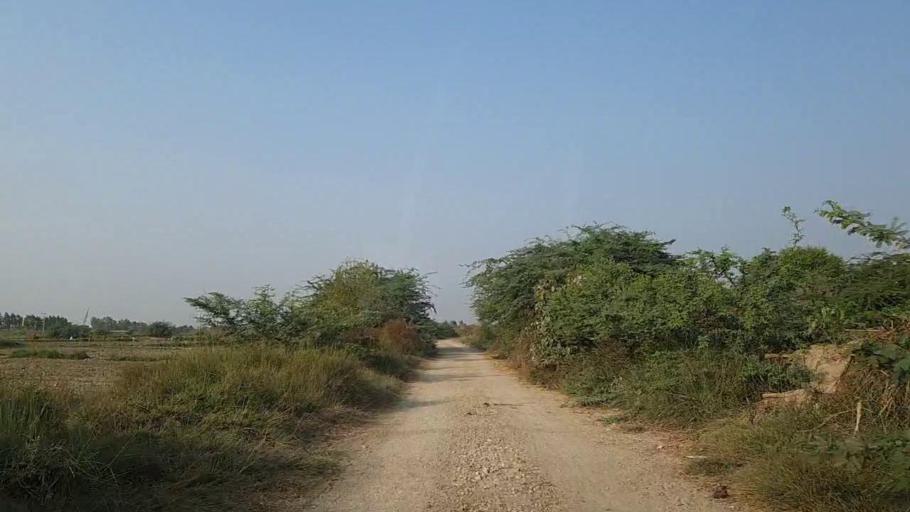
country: PK
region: Sindh
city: Thatta
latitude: 24.6728
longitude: 67.7831
